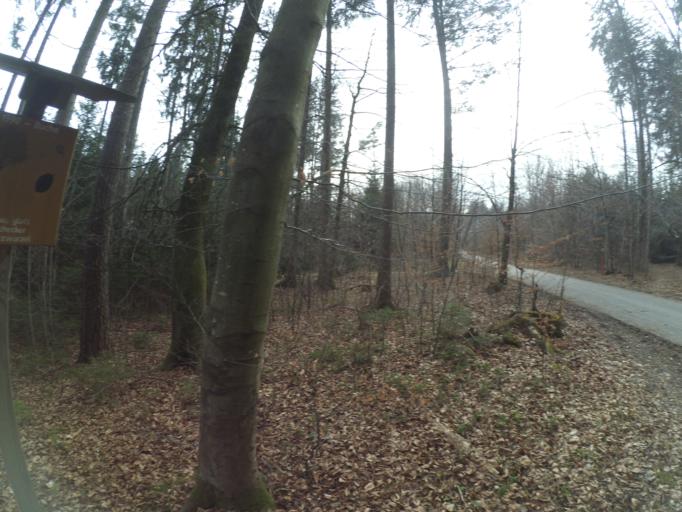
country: DE
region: Bavaria
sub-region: Swabia
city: Bad Worishofen
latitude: 47.9936
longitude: 10.5724
